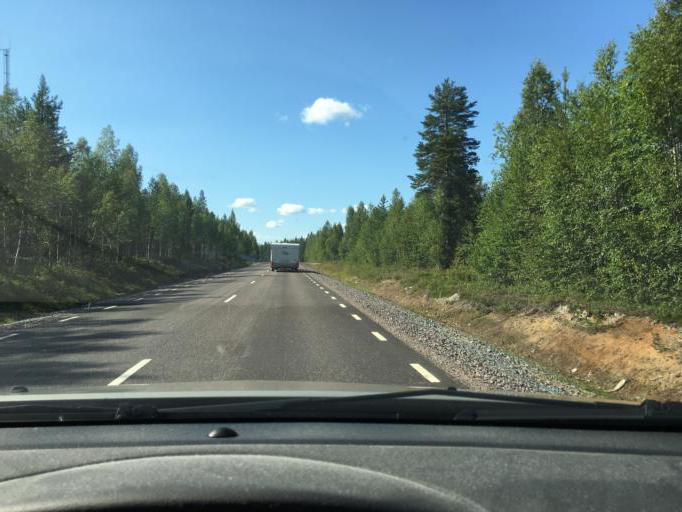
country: SE
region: Norrbotten
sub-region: Lulea Kommun
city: Ranea
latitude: 66.0508
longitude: 22.2256
